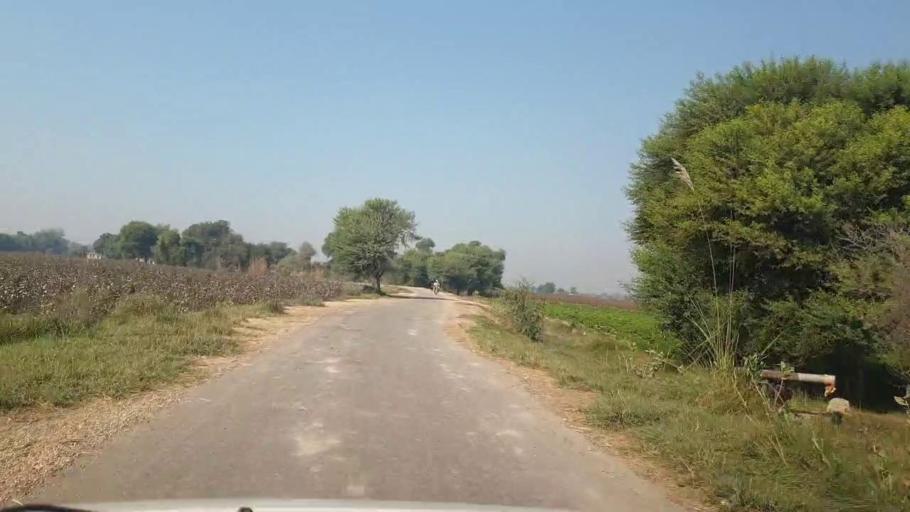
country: PK
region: Sindh
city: Bhan
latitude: 26.6035
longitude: 67.7507
